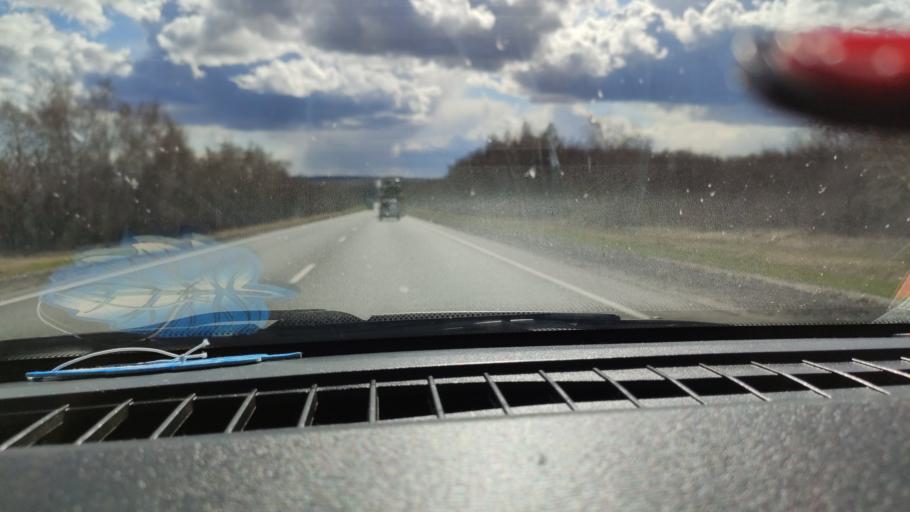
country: RU
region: Saratov
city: Khvalynsk
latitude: 52.5801
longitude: 48.1154
